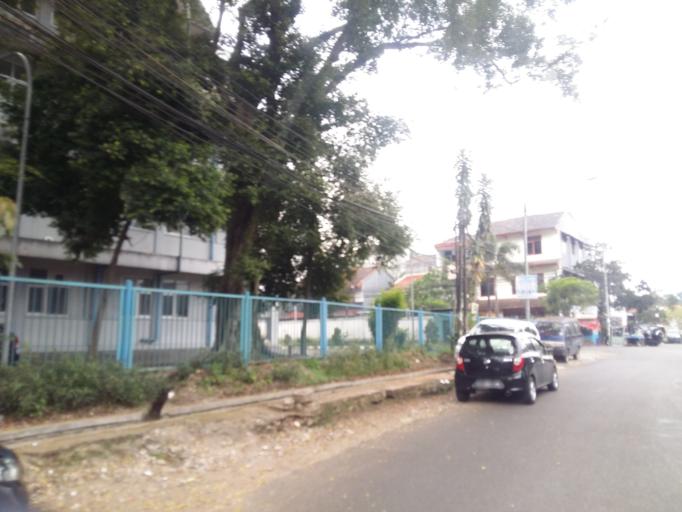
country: ID
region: West Java
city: Bandung
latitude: -6.8830
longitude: 107.6112
